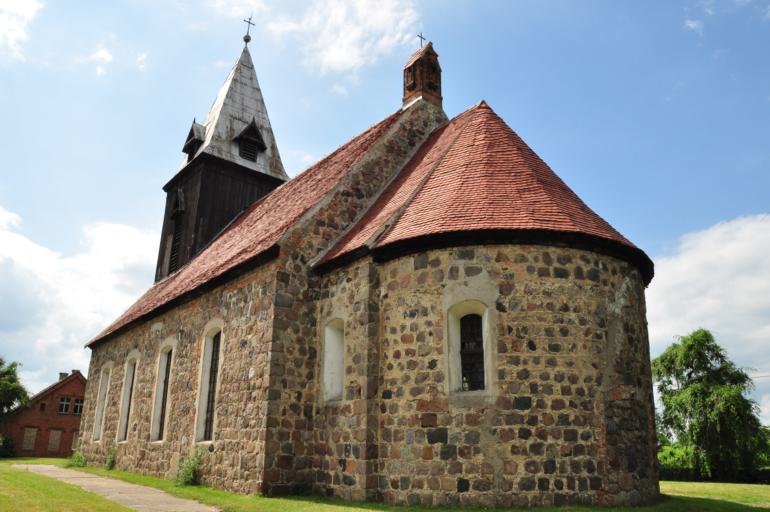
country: PL
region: West Pomeranian Voivodeship
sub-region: Powiat gryfinski
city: Cedynia
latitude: 52.9110
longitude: 14.2623
